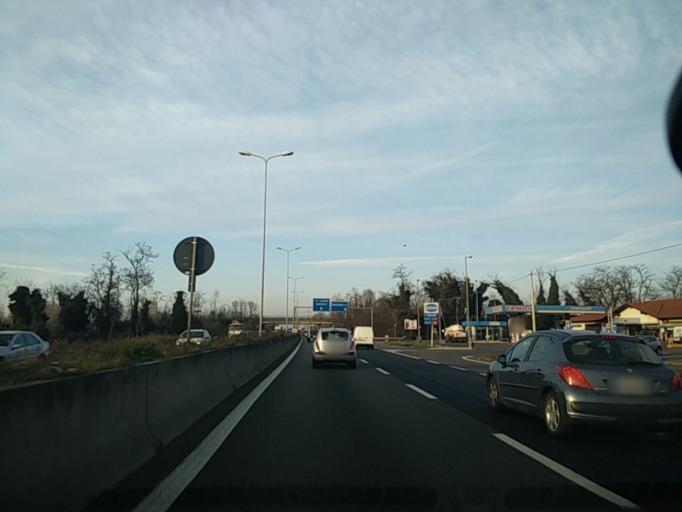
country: IT
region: Lombardy
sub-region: Citta metropolitana di Milano
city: Paderno Dugnano
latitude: 45.5829
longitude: 9.1751
